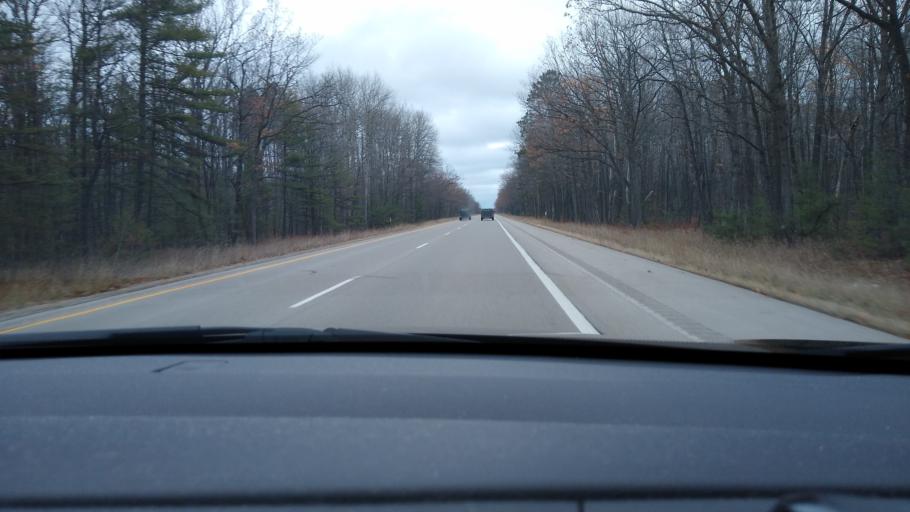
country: US
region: Michigan
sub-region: Cheboygan County
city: Indian River
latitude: 45.4686
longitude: -84.6151
